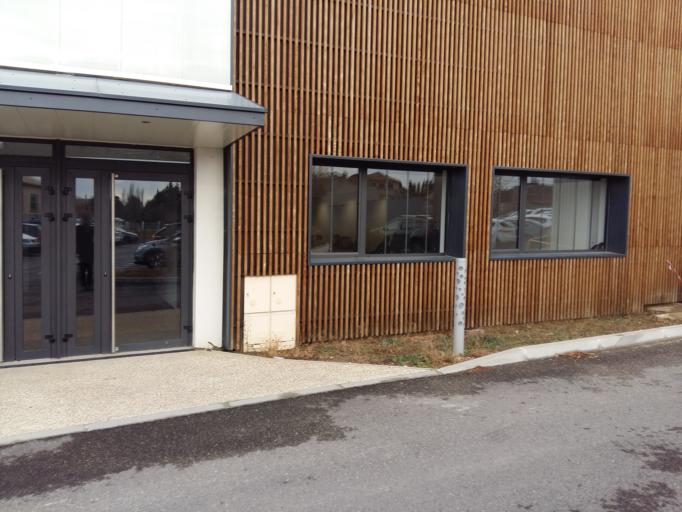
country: FR
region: Provence-Alpes-Cote d'Azur
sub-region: Departement du Vaucluse
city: Valreas
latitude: 44.3857
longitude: 4.9846
